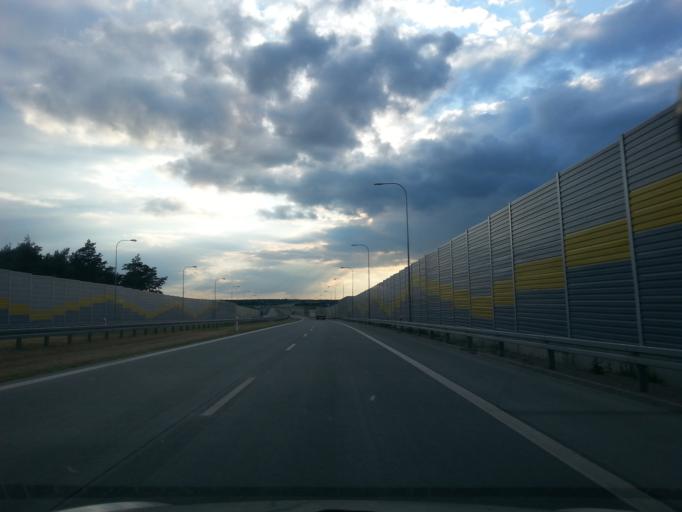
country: PL
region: Lodz Voivodeship
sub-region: Powiat zdunskowolski
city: Zdunska Wola
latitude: 51.5745
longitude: 18.9472
